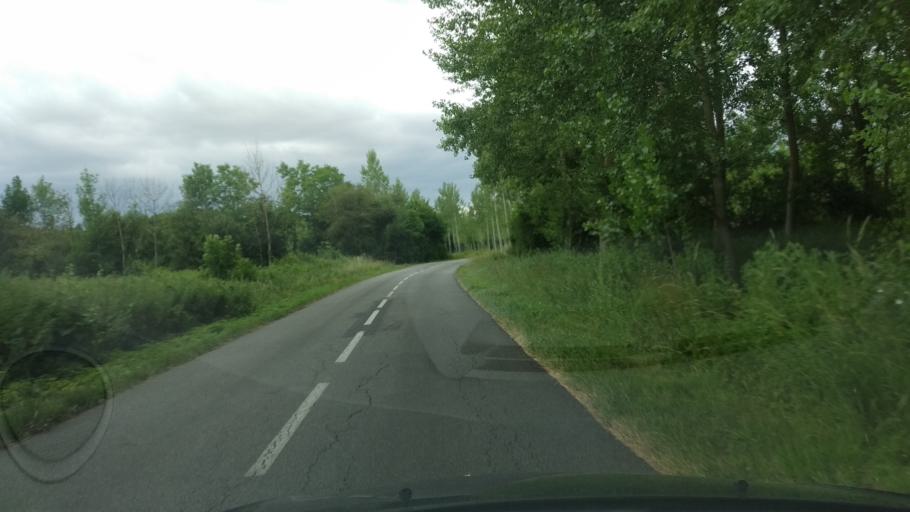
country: FR
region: Poitou-Charentes
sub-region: Departement de la Vienne
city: Vouille
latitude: 46.6319
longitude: 0.1682
